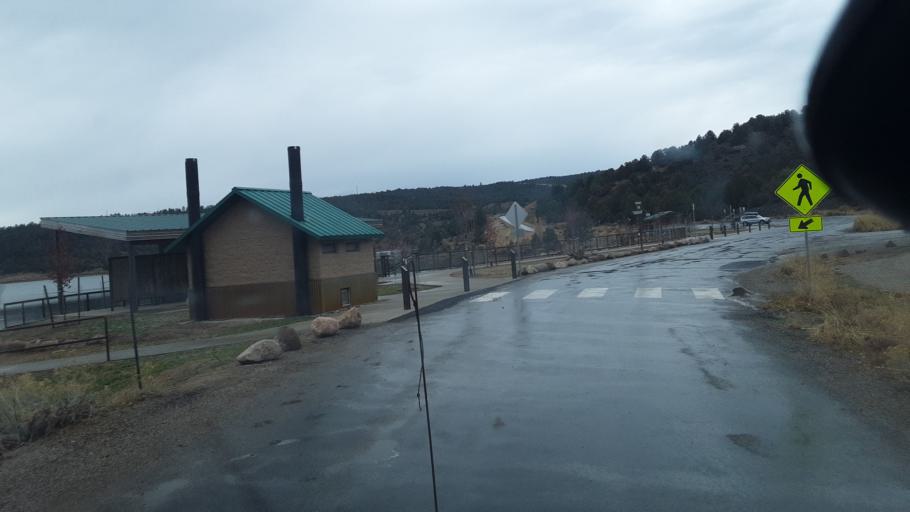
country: US
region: Colorado
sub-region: La Plata County
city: Durango
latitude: 37.2324
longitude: -107.9061
